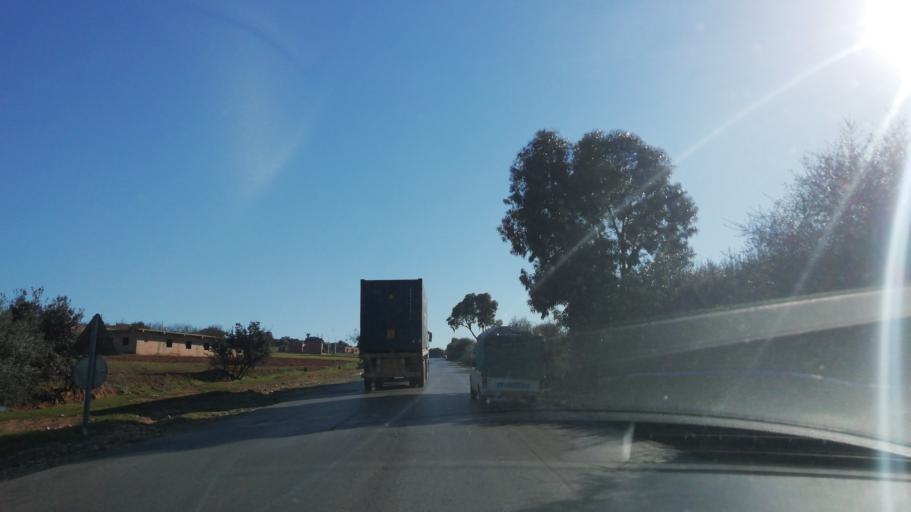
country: DZ
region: Relizane
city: Smala
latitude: 35.6837
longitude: 0.7997
